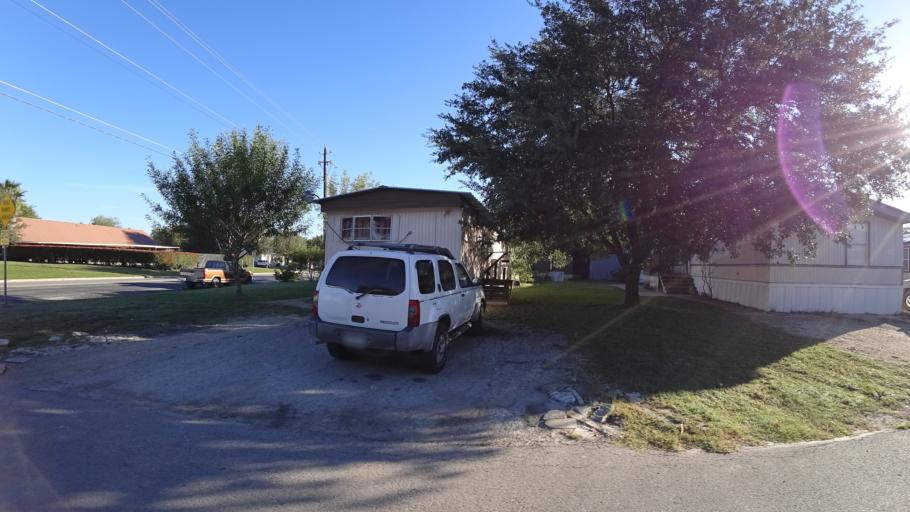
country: US
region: Texas
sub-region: Travis County
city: Austin
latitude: 30.2263
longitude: -97.6934
